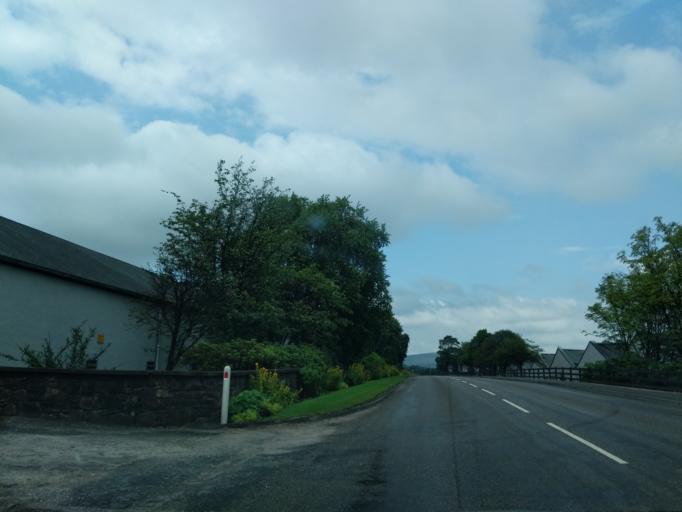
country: GB
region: Scotland
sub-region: Moray
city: Dufftown
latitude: 57.4543
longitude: -3.1306
